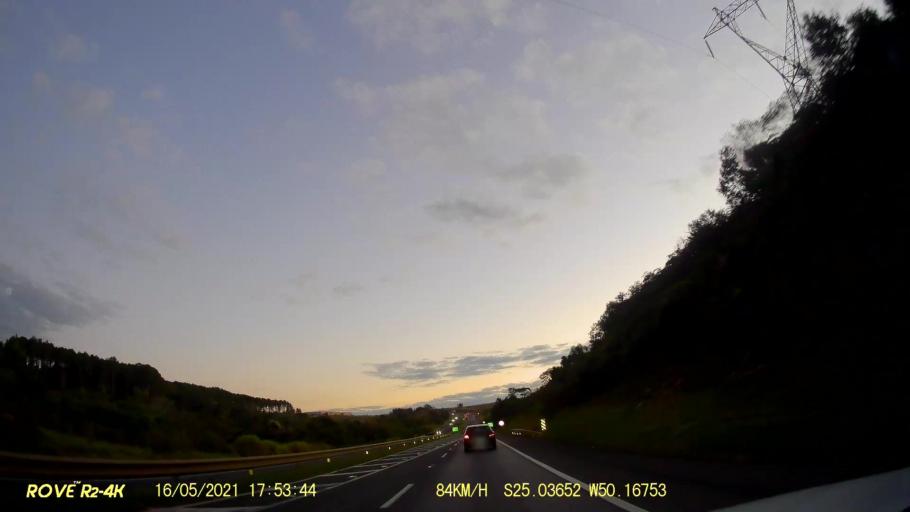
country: BR
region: Parana
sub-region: Ponta Grossa
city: Ponta Grossa
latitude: -25.0365
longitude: -50.1675
